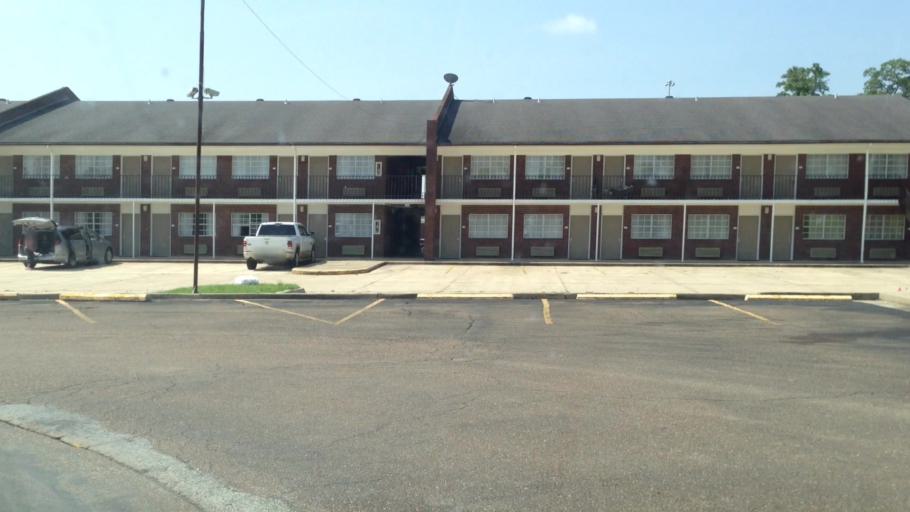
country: US
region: Louisiana
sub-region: Madison Parish
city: Tallulah
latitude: 32.3955
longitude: -91.2005
